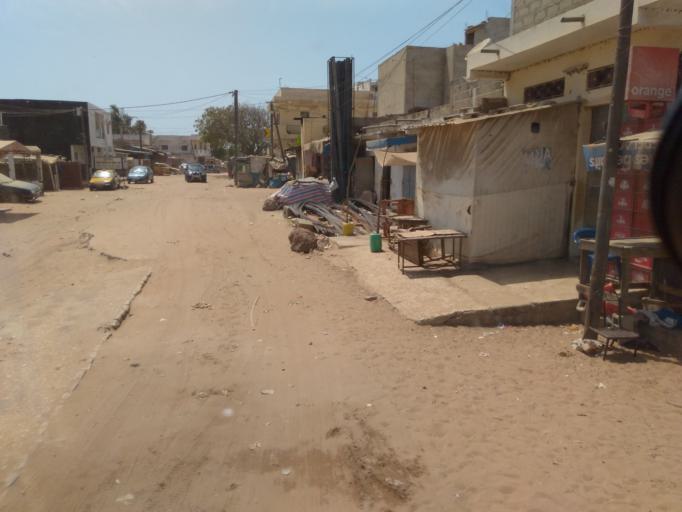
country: SN
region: Dakar
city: Pikine
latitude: 14.7879
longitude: -17.3382
